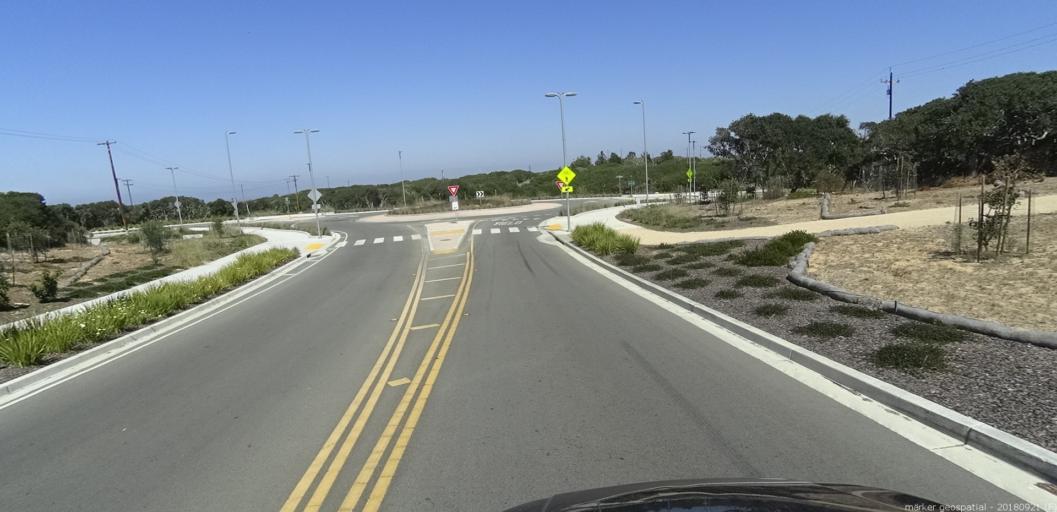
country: US
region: California
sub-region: Monterey County
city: Marina
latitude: 36.6540
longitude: -121.7859
